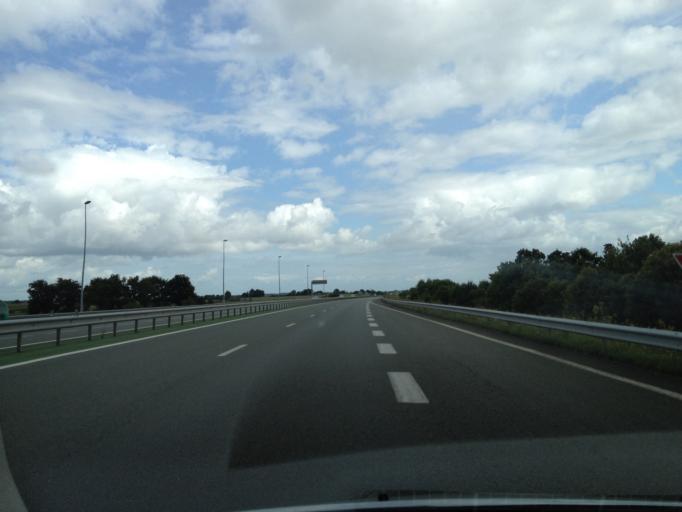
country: FR
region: Pays de la Loire
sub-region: Departement de Maine-et-Loire
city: Trementines
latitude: 47.1381
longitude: -0.8240
